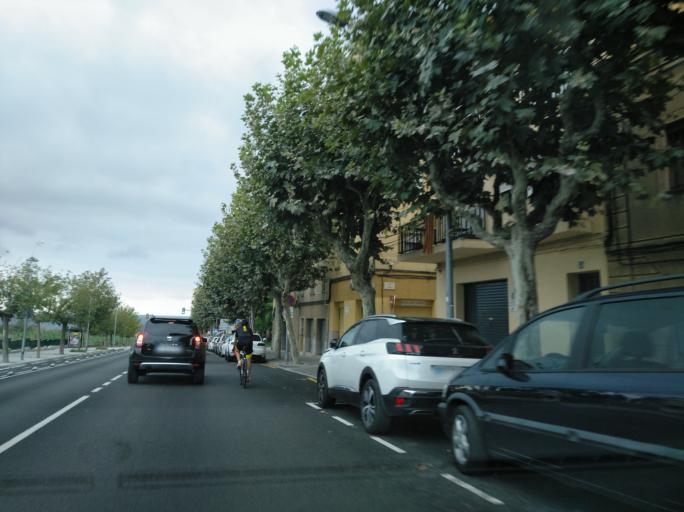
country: ES
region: Catalonia
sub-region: Provincia de Barcelona
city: Mataro
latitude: 41.5447
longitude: 2.4546
